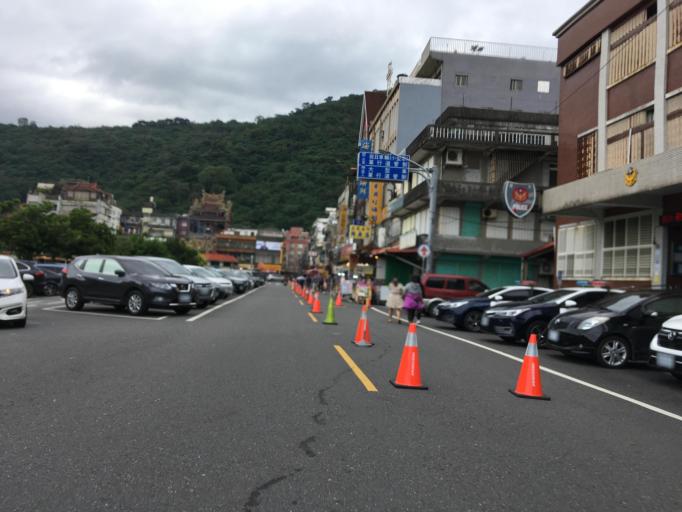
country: TW
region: Taiwan
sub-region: Yilan
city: Yilan
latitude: 24.5823
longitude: 121.8663
